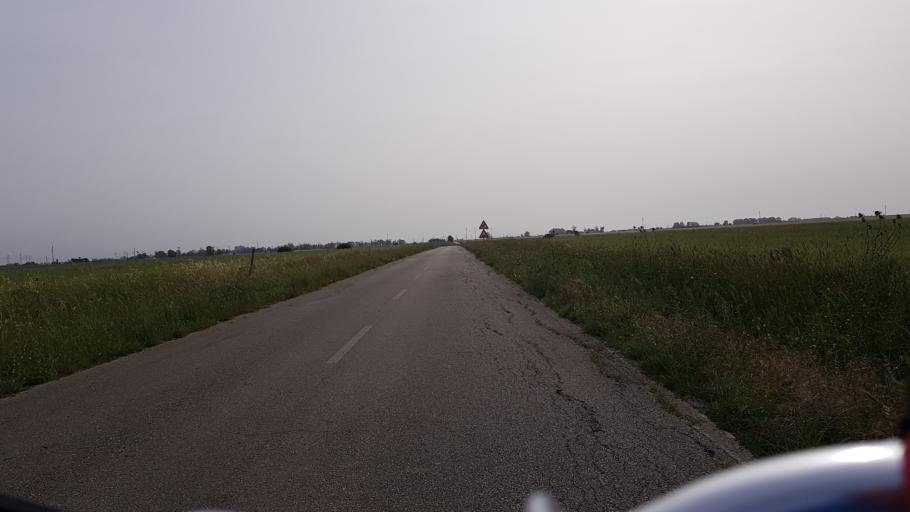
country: IT
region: Apulia
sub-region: Provincia di Brindisi
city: La Rosa
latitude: 40.5796
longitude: 18.0273
